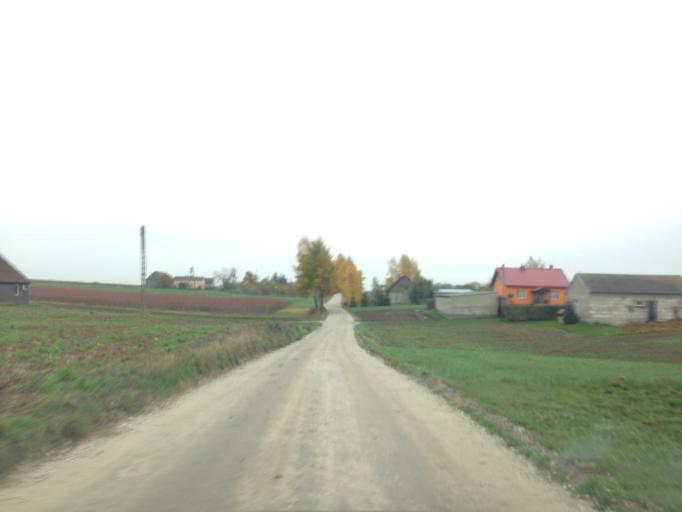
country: PL
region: Kujawsko-Pomorskie
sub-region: Powiat brodnicki
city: Bartniczka
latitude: 53.2142
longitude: 19.5613
